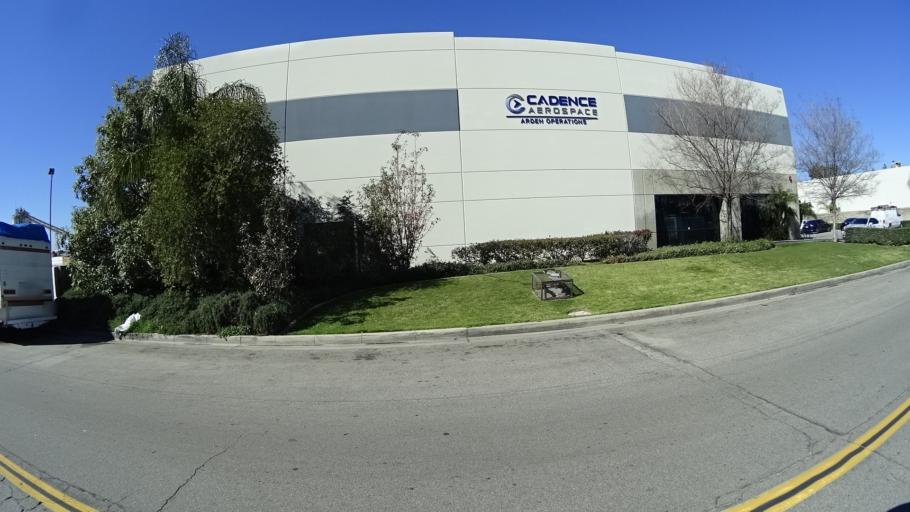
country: US
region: California
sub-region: Orange County
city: Orange
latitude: 33.8178
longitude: -117.8675
